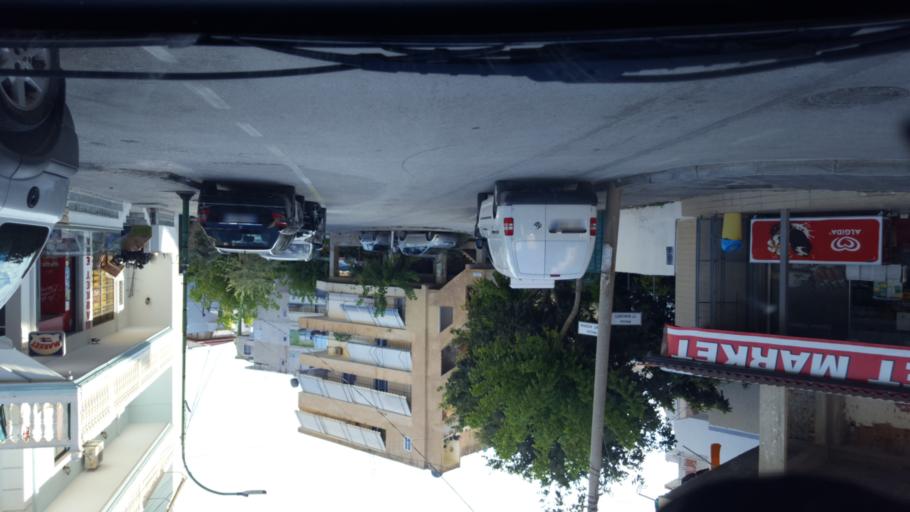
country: AL
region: Vlore
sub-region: Rrethi i Sarandes
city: Sarande
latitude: 39.8703
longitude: 19.9992
